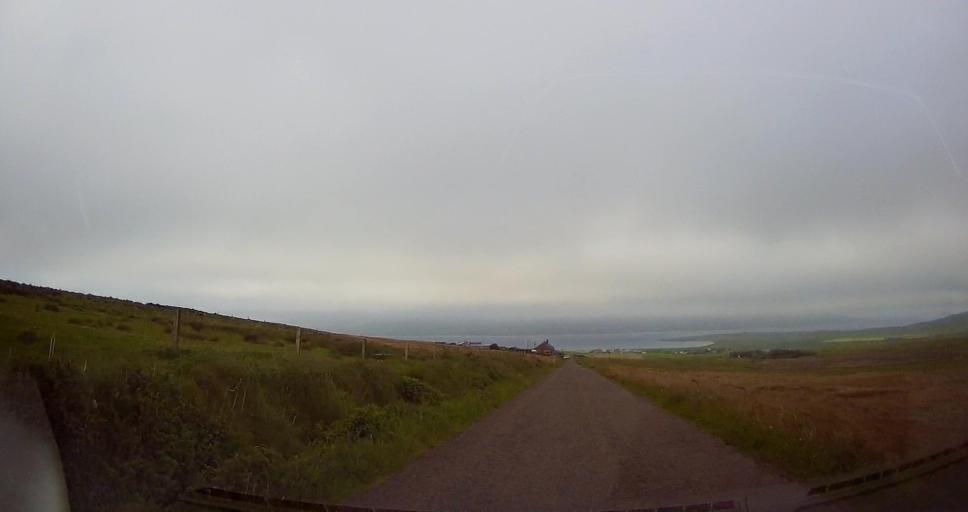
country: GB
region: Scotland
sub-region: Orkney Islands
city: Orkney
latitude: 59.1056
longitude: -3.1280
